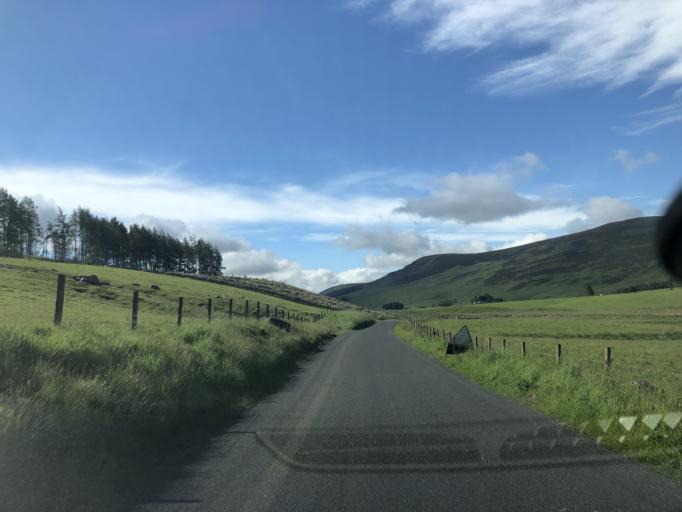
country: GB
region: Scotland
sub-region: Angus
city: Kirriemuir
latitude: 56.8030
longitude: -3.0374
